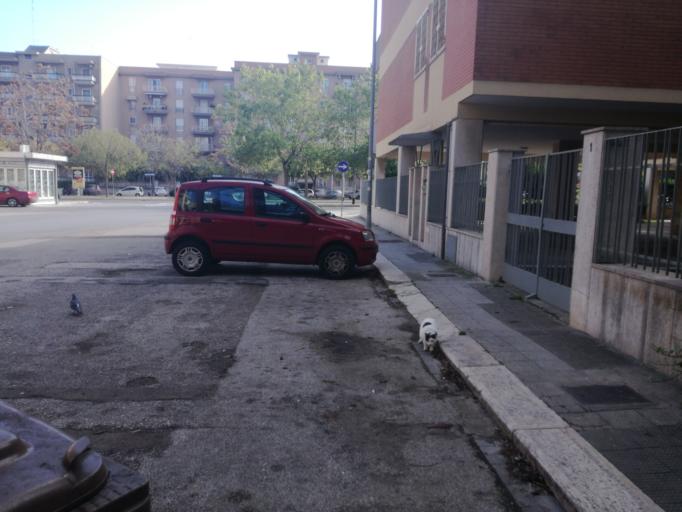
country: IT
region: Apulia
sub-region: Provincia di Bari
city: Bari
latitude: 41.1127
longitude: 16.8914
